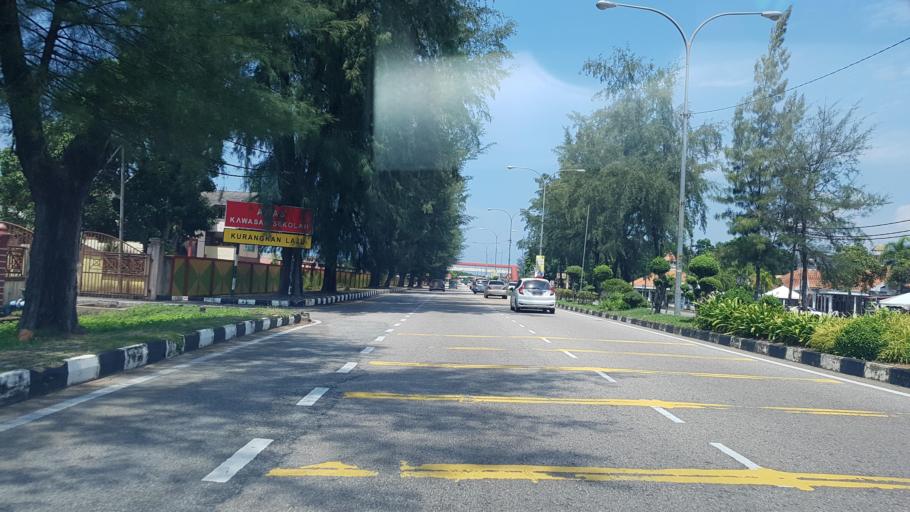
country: MY
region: Terengganu
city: Kuala Terengganu
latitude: 5.3015
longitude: 103.1622
